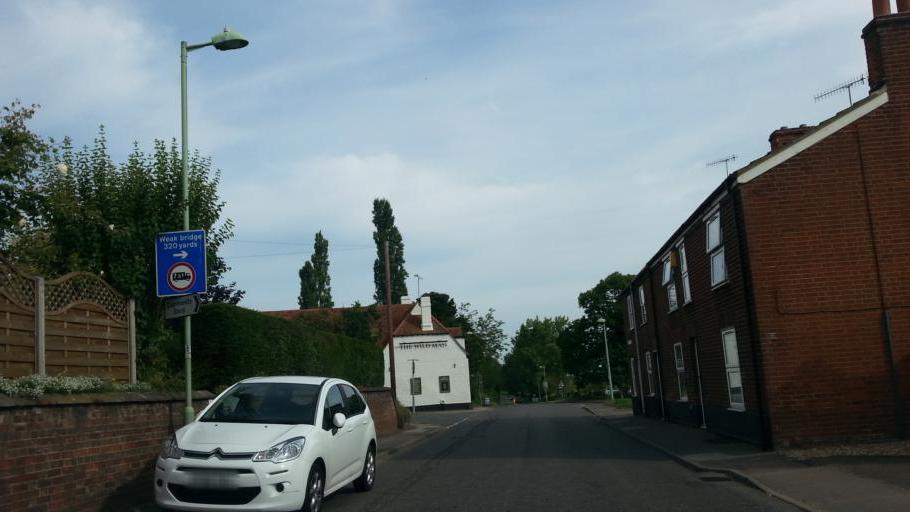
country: GB
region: England
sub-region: Suffolk
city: Bramford
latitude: 52.0620
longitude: 1.0950
